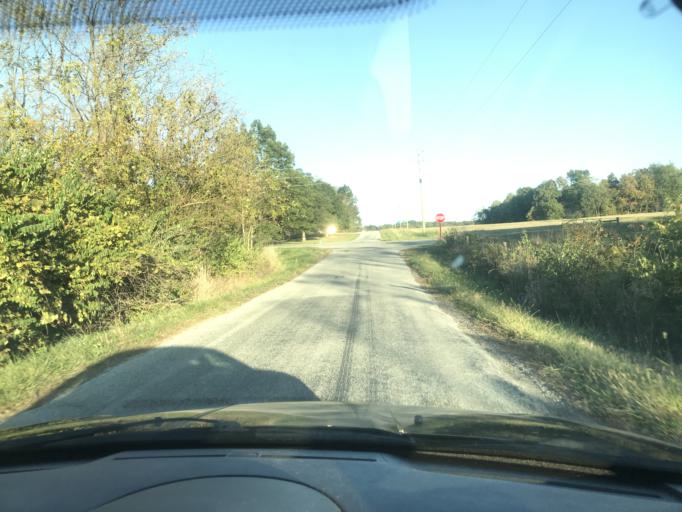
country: US
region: Ohio
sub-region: Logan County
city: West Liberty
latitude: 40.2312
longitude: -83.7974
